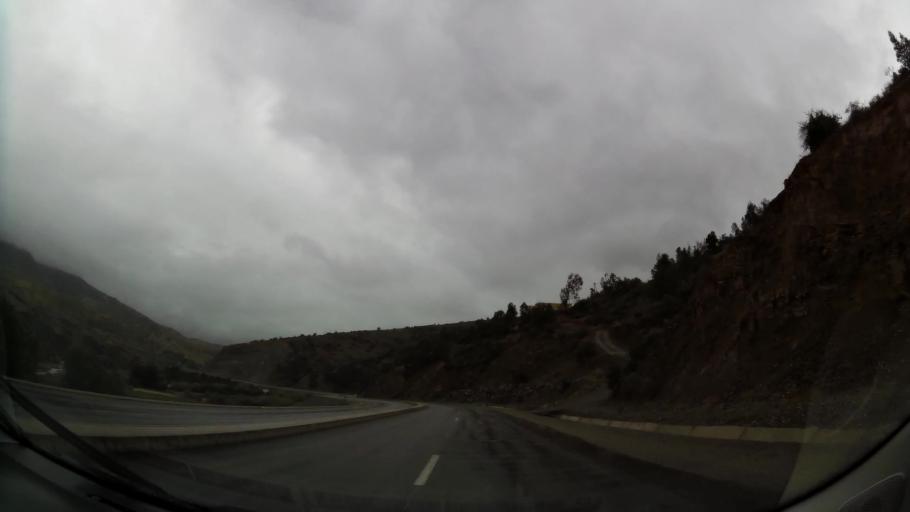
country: MA
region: Taza-Al Hoceima-Taounate
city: Imzourene
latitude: 35.0113
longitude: -3.8167
